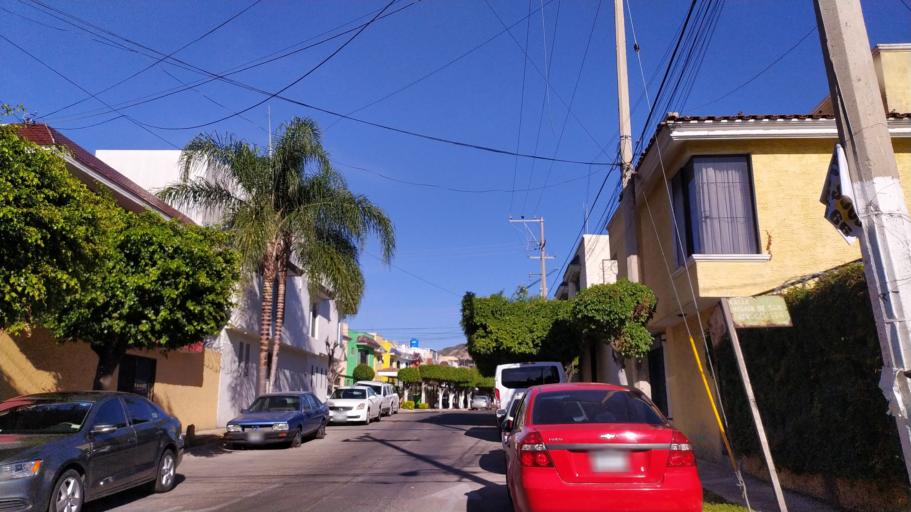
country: MX
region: Jalisco
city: Guadalajara
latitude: 20.6541
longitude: -103.4364
